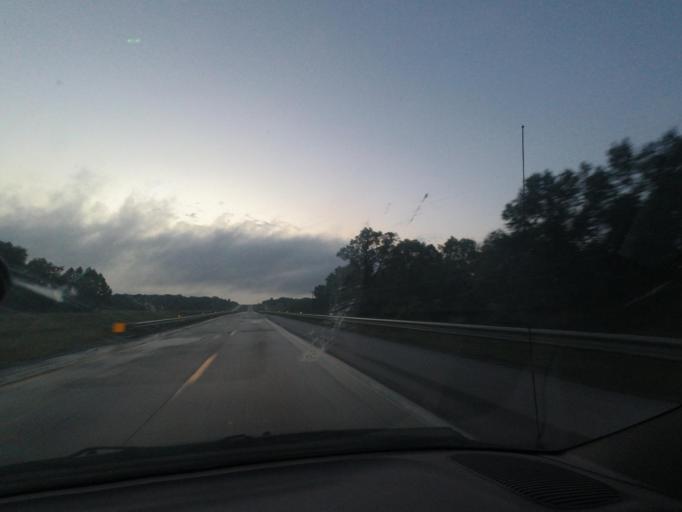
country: US
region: Missouri
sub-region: Linn County
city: Brookfield
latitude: 39.7639
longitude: -93.0381
